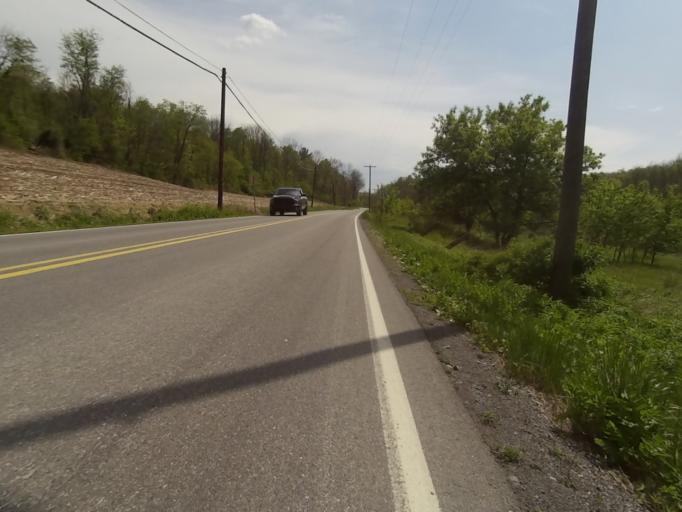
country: US
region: Pennsylvania
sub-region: Centre County
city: Zion
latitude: 40.9930
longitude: -77.6410
